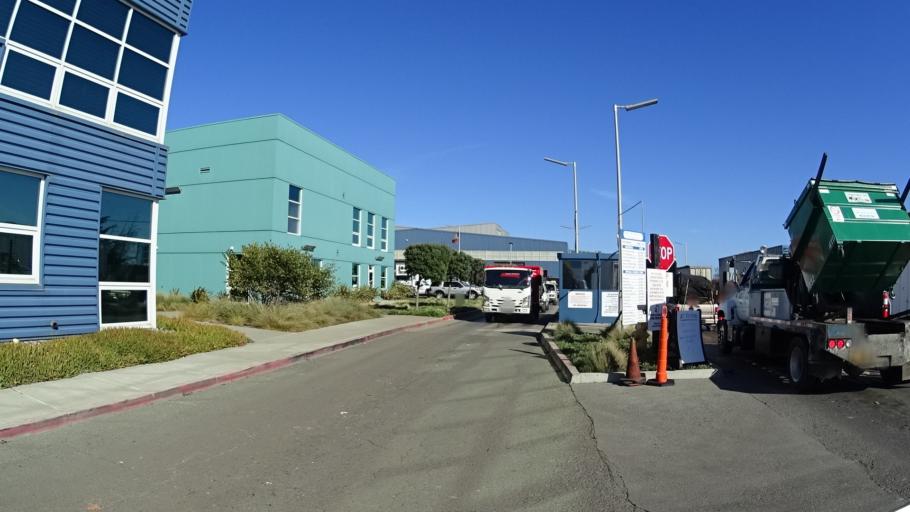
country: US
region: California
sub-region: San Mateo County
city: South San Francisco
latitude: 37.6484
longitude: -122.3835
